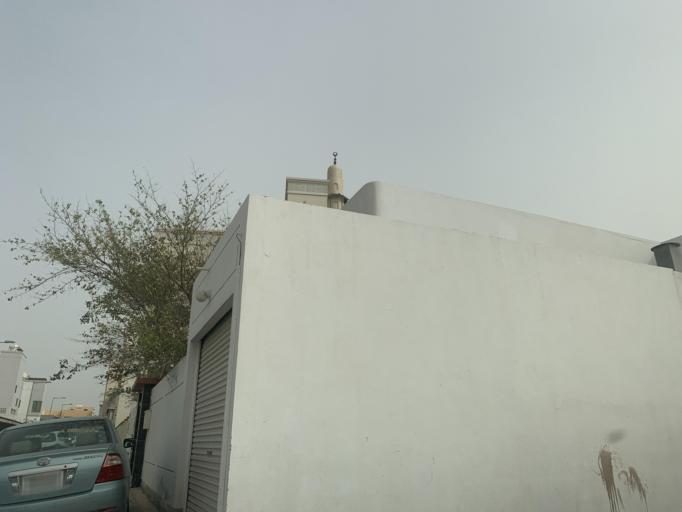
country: BH
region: Northern
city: Madinat `Isa
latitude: 26.1579
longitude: 50.5699
